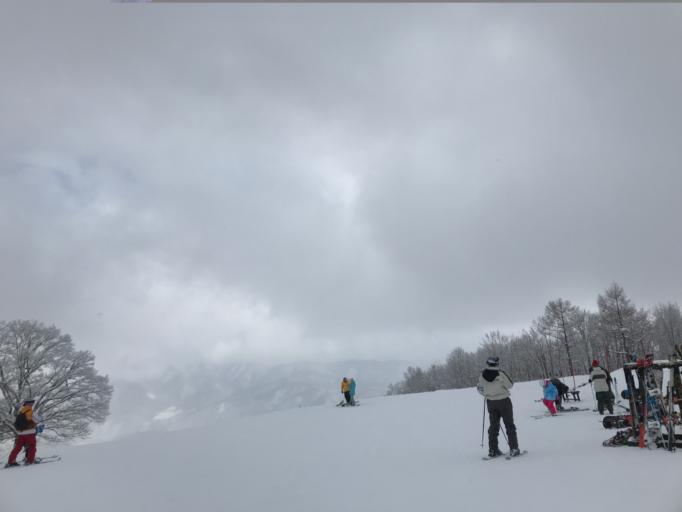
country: JP
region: Nagano
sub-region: Kitaazumi Gun
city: Hakuba
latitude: 36.7098
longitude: 137.8194
